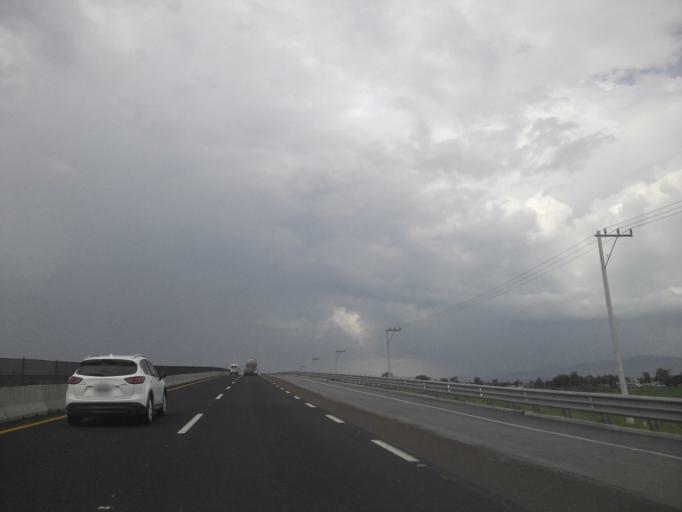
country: MX
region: Hidalgo
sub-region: Tula de Allende
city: Residencial Arboledas
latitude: 20.0953
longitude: -99.2974
